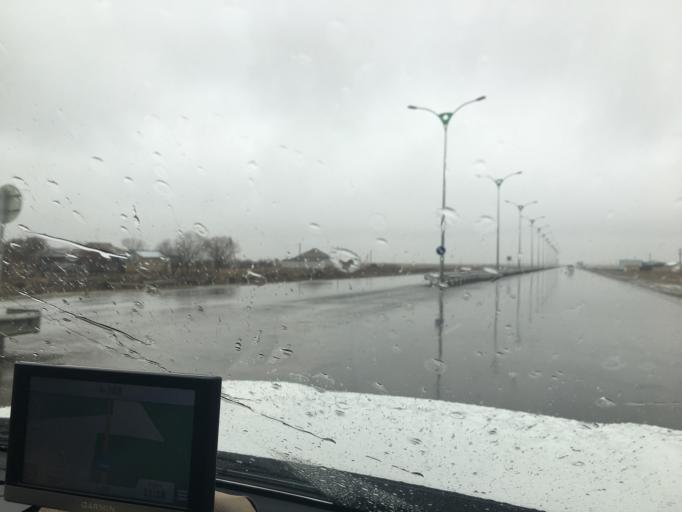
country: TM
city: Murgab
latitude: 37.4878
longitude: 61.9877
